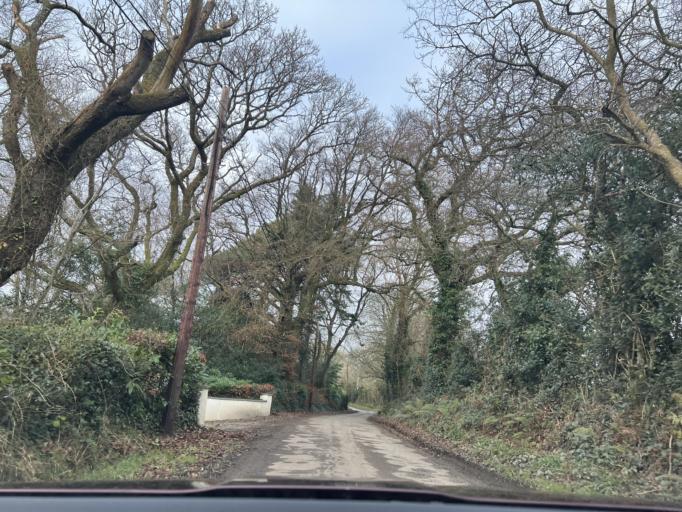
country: IE
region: Leinster
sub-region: Loch Garman
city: Castlebridge
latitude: 52.3771
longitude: -6.5439
